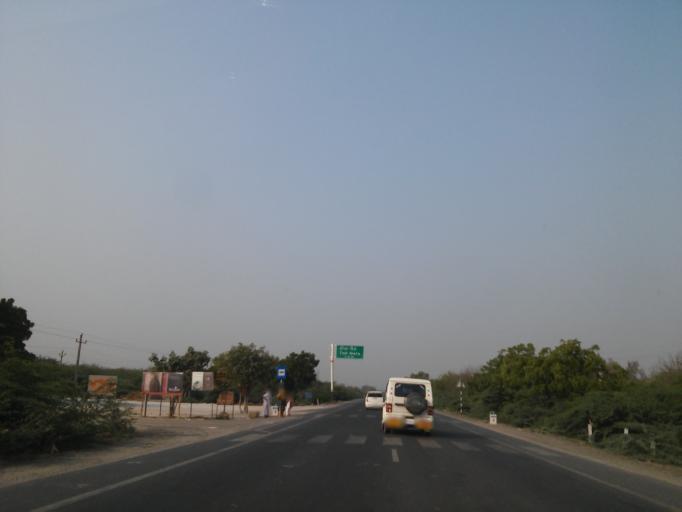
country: IN
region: Gujarat
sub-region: Kachchh
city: Bhuj
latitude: 23.2390
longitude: 69.8025
